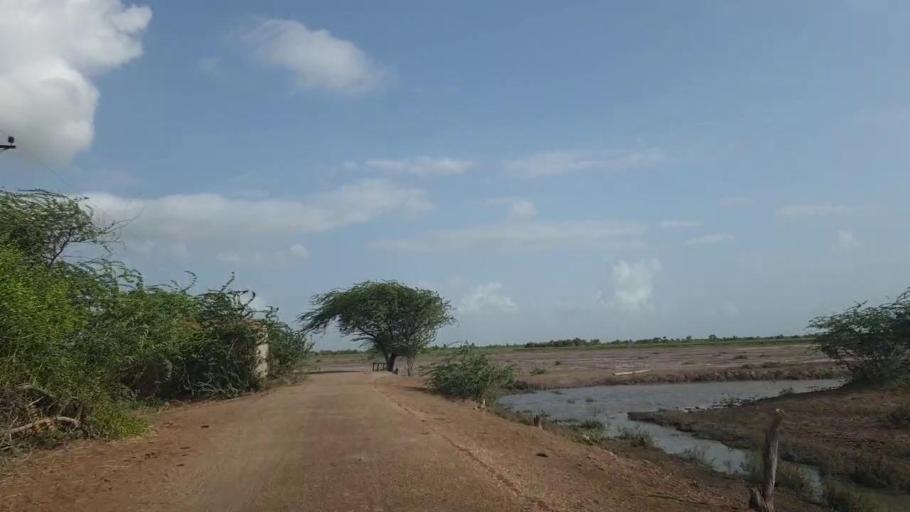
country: PK
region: Sindh
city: Kadhan
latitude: 24.6304
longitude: 69.0812
